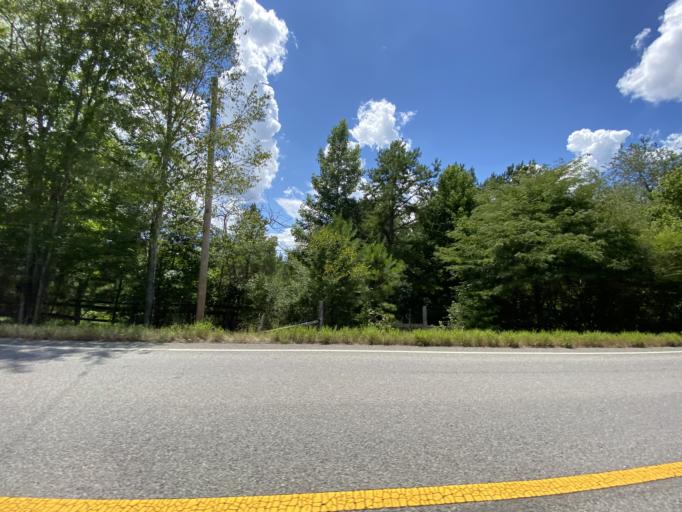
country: US
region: Alabama
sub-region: Lauderdale County
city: Underwood-Petersville
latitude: 34.9605
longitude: -87.8805
